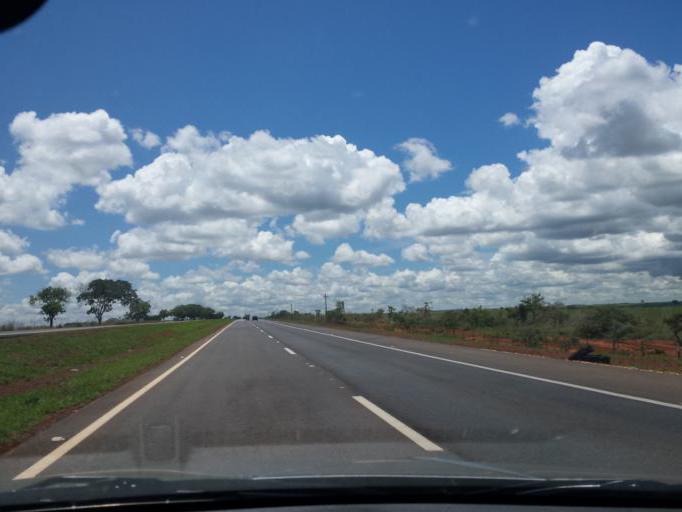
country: BR
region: Goias
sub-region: Cristalina
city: Cristalina
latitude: -16.6958
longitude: -47.6954
